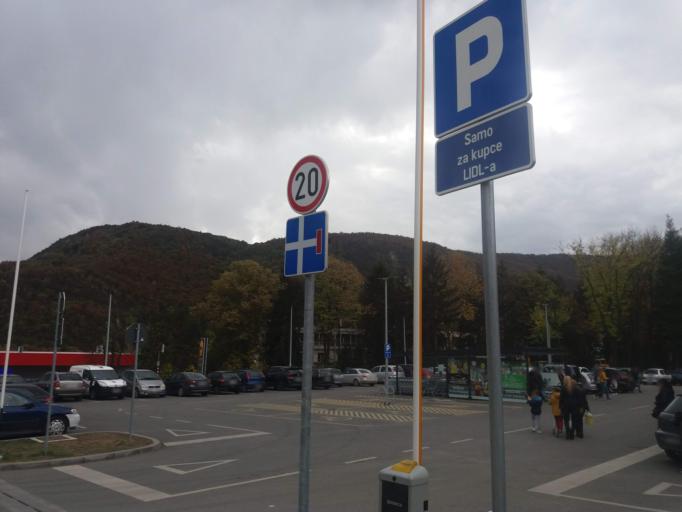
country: RS
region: Central Serbia
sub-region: Zlatiborski Okrug
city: Uzice
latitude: 43.8528
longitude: 19.8558
